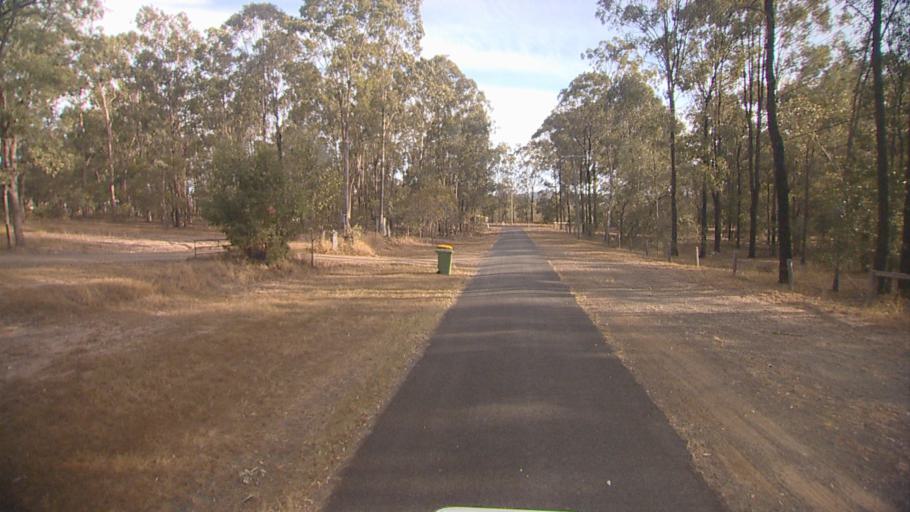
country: AU
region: Queensland
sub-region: Logan
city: Cedar Vale
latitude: -27.8747
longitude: 153.0275
